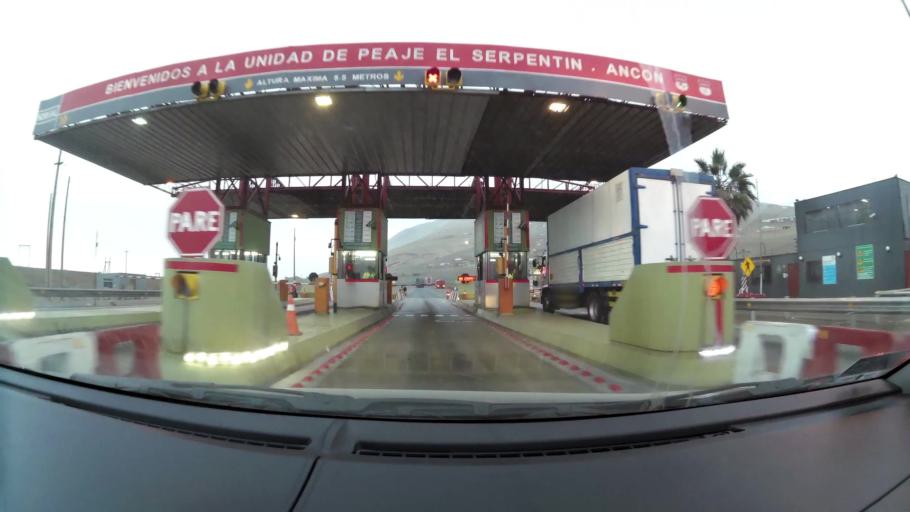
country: PE
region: Lima
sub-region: Lima
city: Santa Rosa
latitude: -11.7440
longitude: -77.1649
